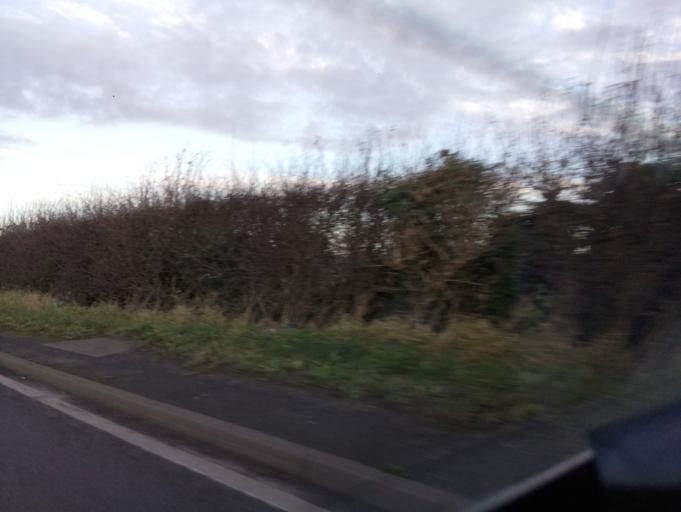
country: GB
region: England
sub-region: Staffordshire
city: Stone
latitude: 52.8647
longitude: -2.1313
